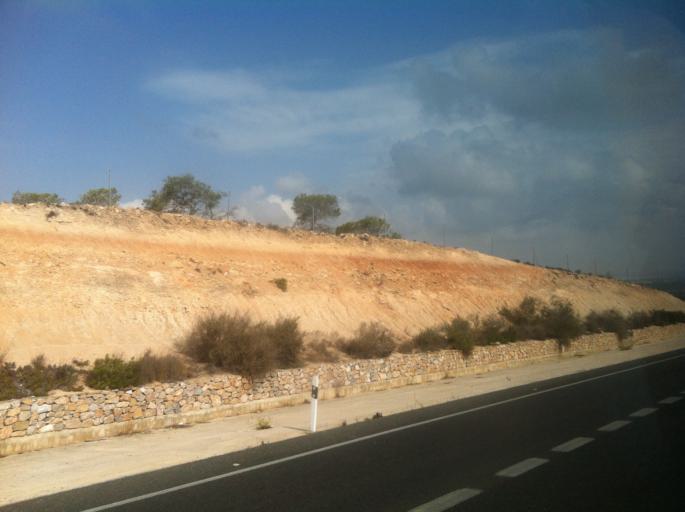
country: ES
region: Valencia
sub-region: Provincia de Alicante
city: Guardamar del Segura
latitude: 38.1516
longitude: -0.6573
